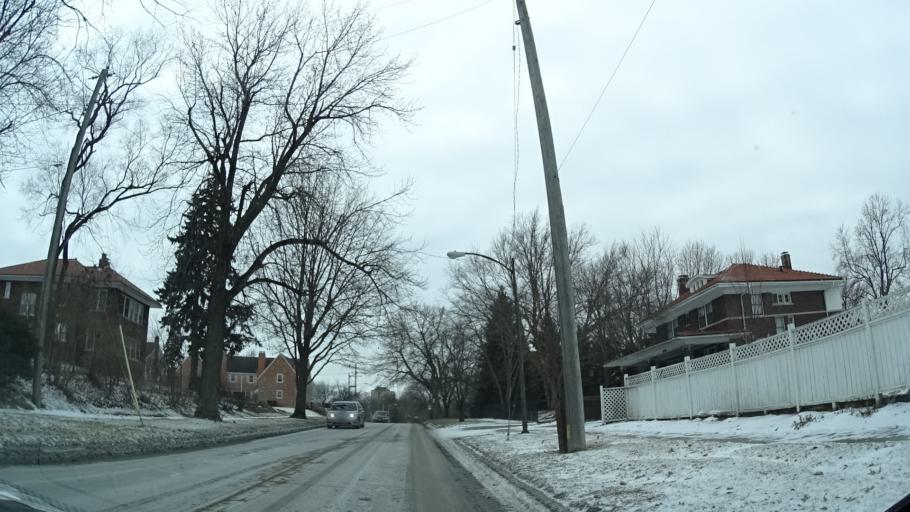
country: US
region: Nebraska
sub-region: Douglas County
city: Omaha
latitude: 41.2612
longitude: -95.9951
